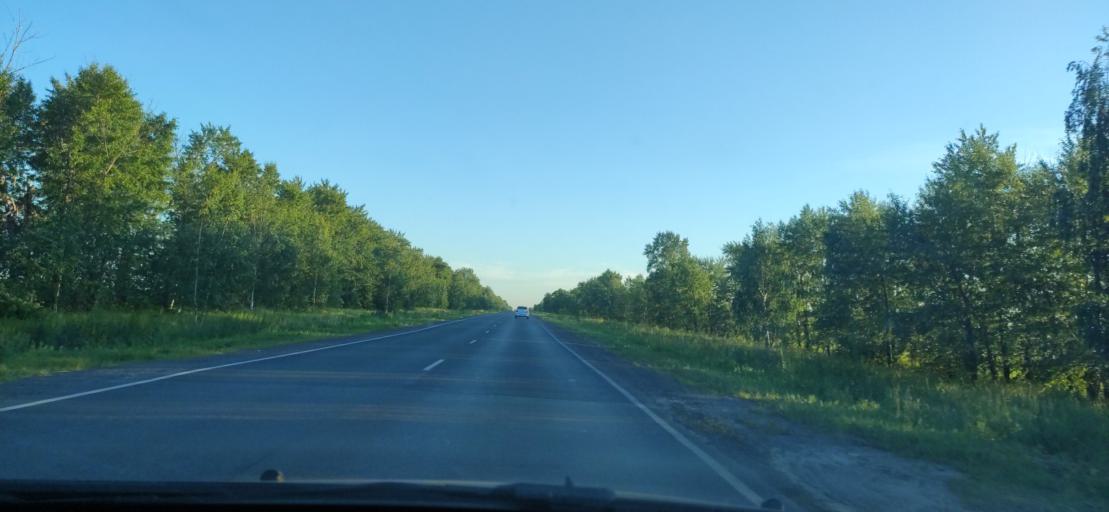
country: RU
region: Ulyanovsk
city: Cherdakly
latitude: 54.4115
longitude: 48.8795
